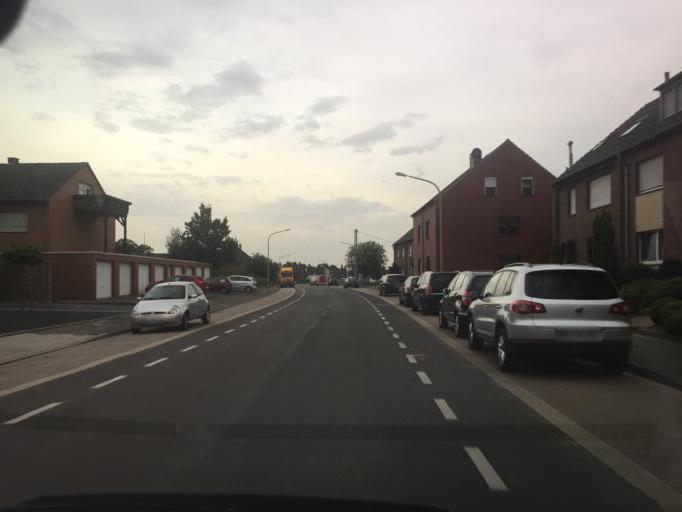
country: DE
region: North Rhine-Westphalia
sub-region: Regierungsbezirk Dusseldorf
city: Monchengladbach
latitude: 51.1760
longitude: 6.3717
